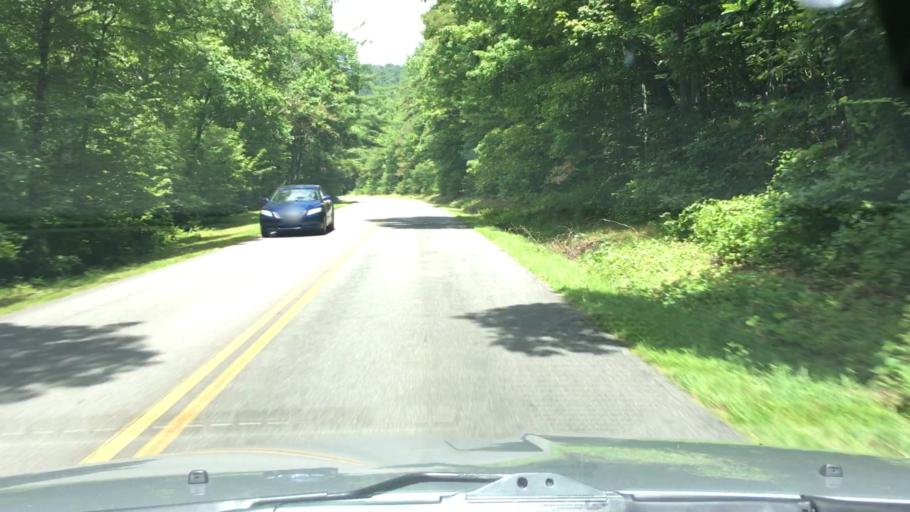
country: US
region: North Carolina
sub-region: Buncombe County
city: Asheville
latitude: 35.6264
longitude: -82.4925
